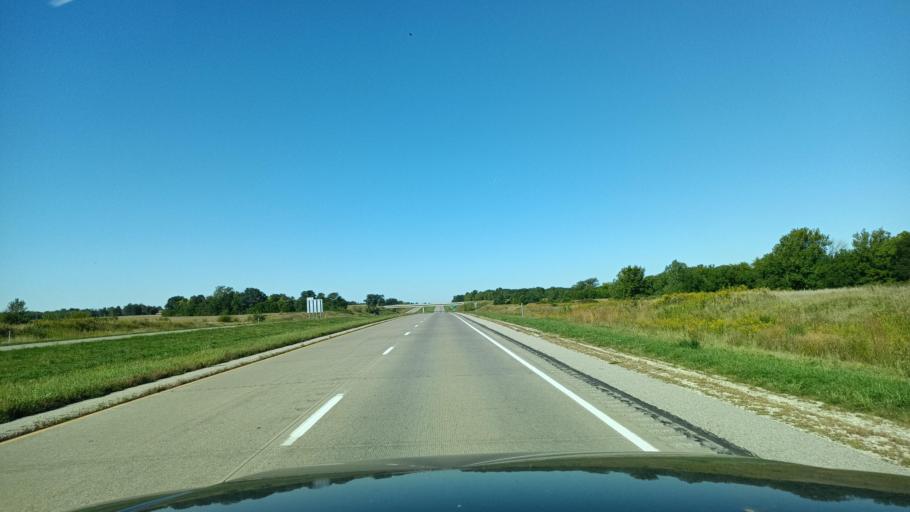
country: US
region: Iowa
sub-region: Lee County
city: Fort Madison
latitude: 40.6707
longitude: -91.2941
